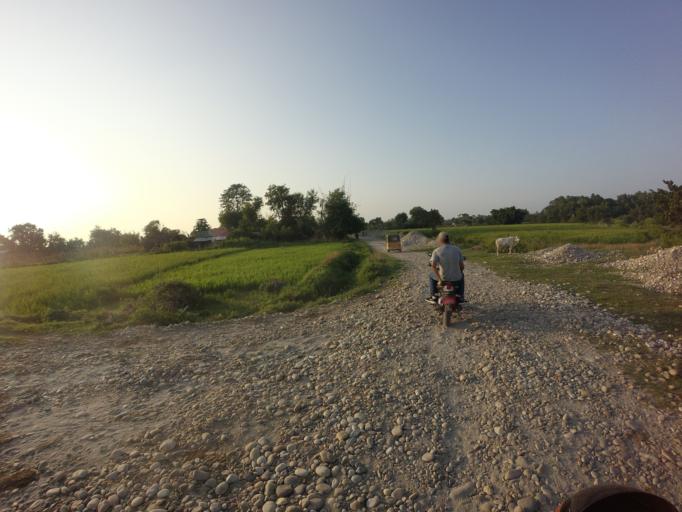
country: NP
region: Far Western
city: Tikapur
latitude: 28.4513
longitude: 81.0731
